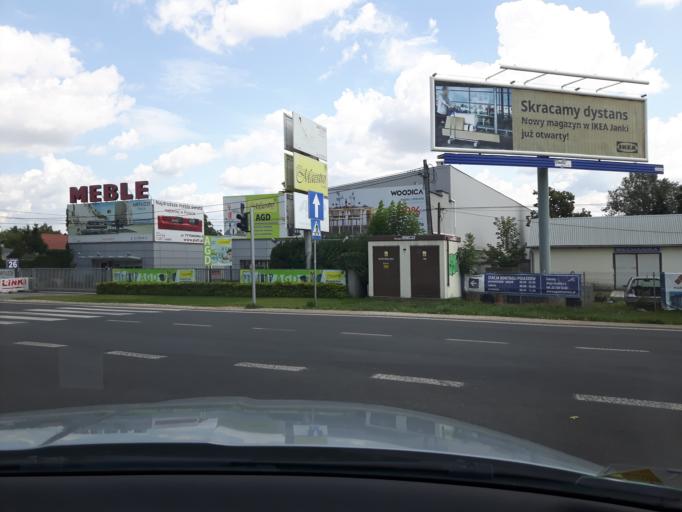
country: PL
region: Masovian Voivodeship
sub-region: Powiat pruszkowski
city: Nowe Grocholice
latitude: 52.1320
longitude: 20.8978
